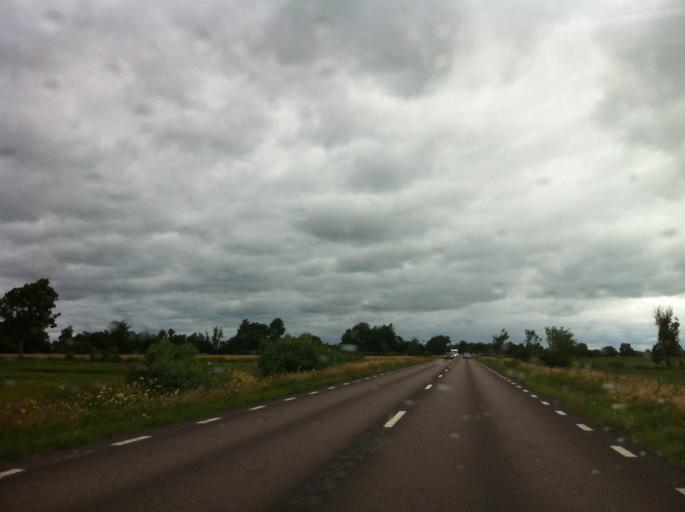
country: SE
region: Kalmar
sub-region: Borgholms Kommun
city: Borgholm
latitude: 57.1267
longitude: 16.9703
